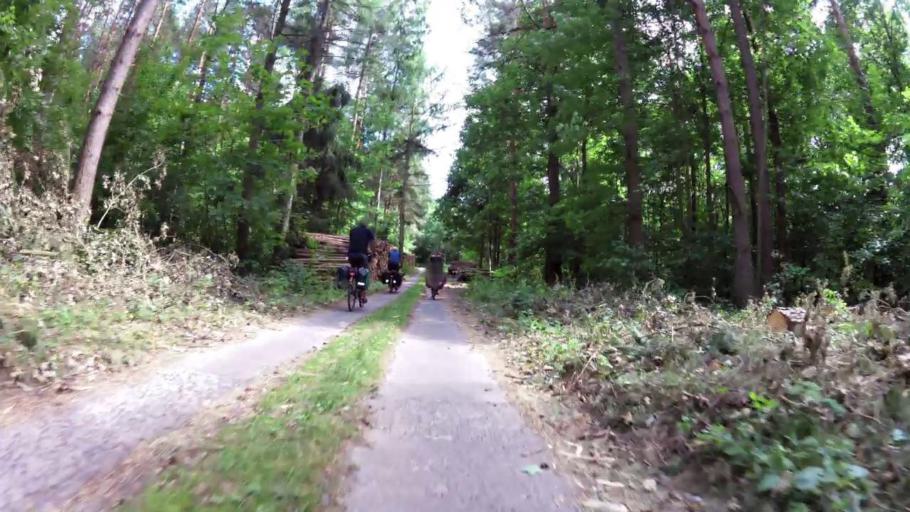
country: PL
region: West Pomeranian Voivodeship
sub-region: Powiat lobeski
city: Lobez
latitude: 53.6523
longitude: 15.5783
